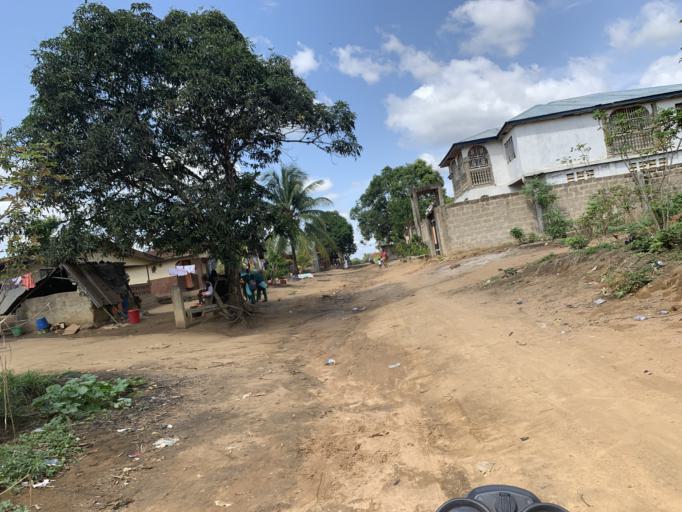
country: SL
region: Western Area
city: Waterloo
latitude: 8.3342
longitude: -13.0501
